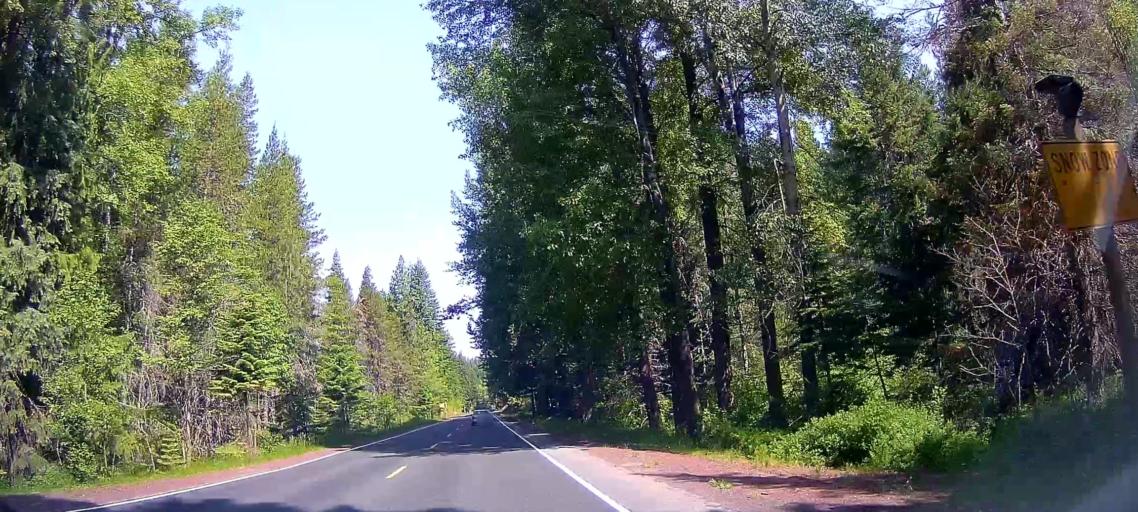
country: US
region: Oregon
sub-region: Clackamas County
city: Mount Hood Village
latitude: 45.1208
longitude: -121.5832
